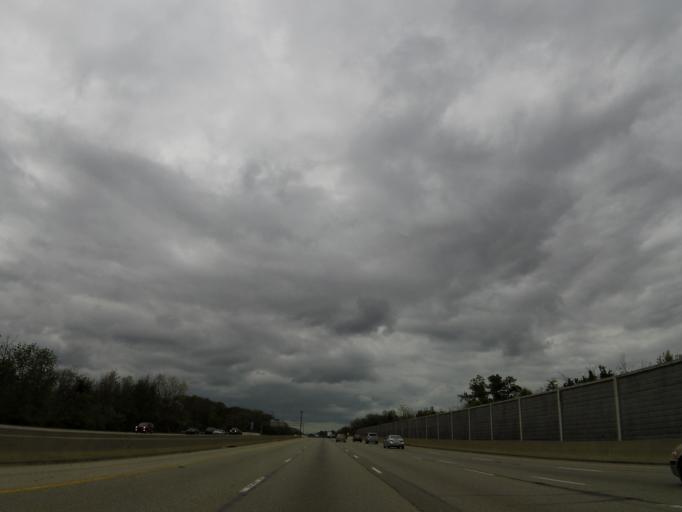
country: US
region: Ohio
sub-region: Hamilton County
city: Highpoint
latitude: 39.2762
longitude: -84.3432
